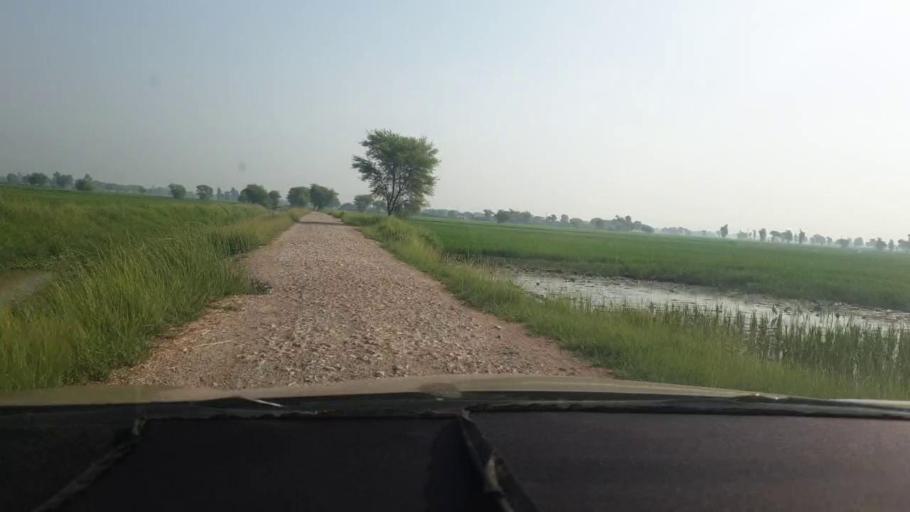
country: PK
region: Sindh
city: Kambar
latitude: 27.5901
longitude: 68.1050
